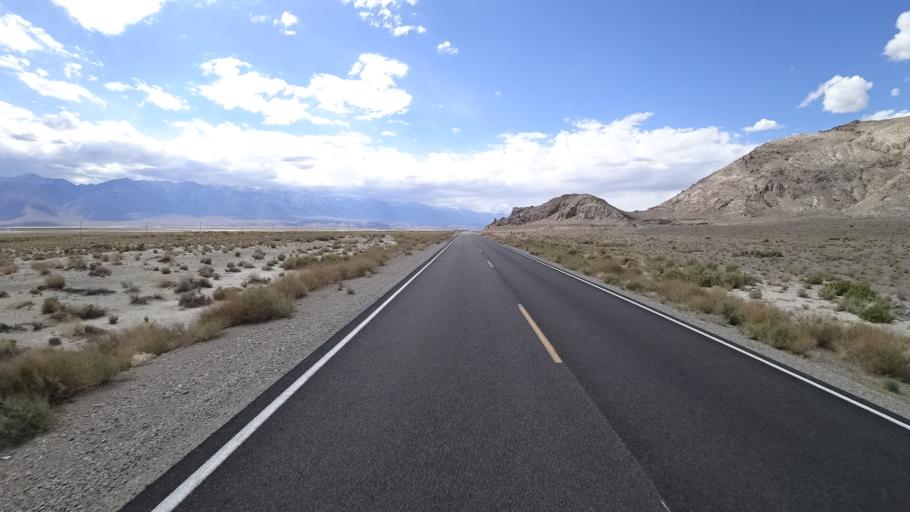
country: US
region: California
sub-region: Inyo County
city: Lone Pine
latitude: 36.5332
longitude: -117.9199
